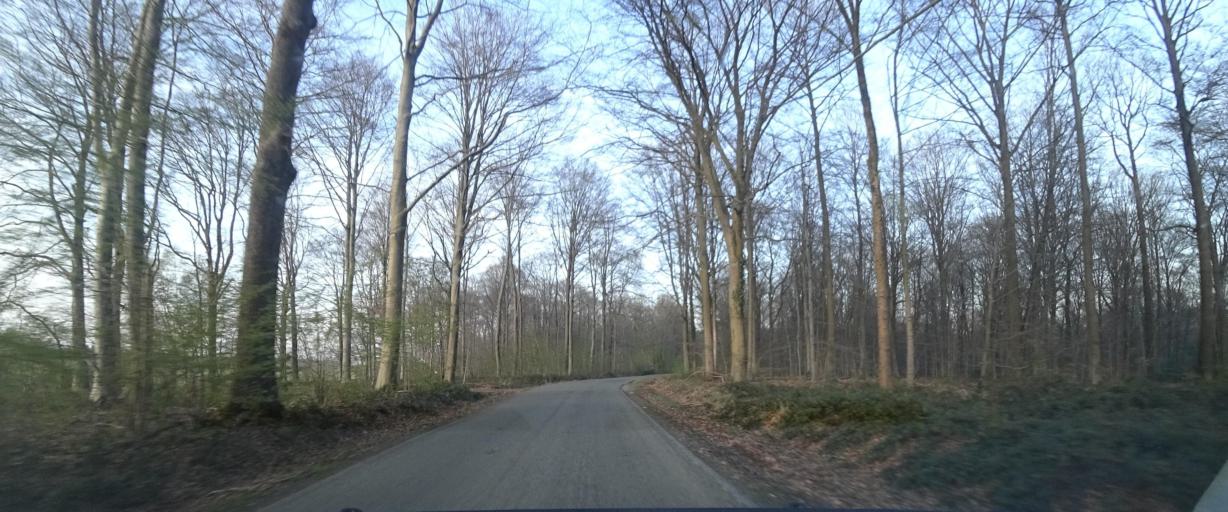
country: BE
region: Wallonia
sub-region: Province de Namur
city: Hamois
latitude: 50.3309
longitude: 5.2174
